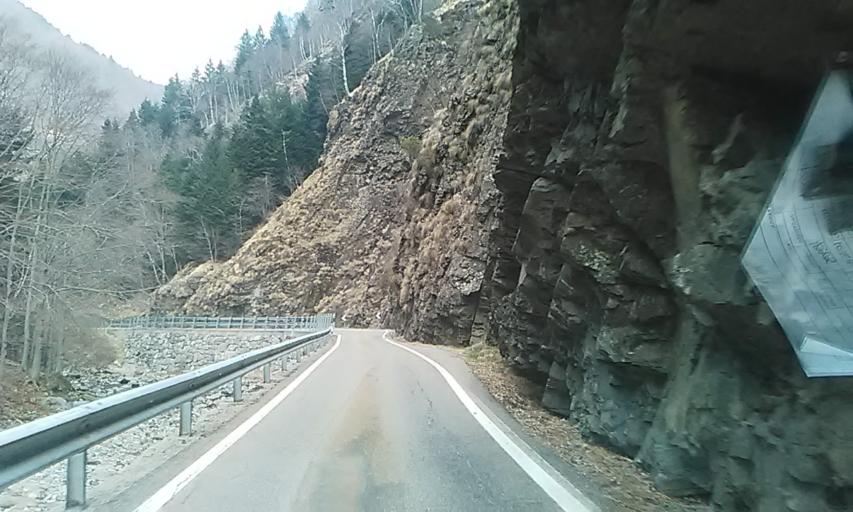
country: IT
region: Piedmont
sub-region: Provincia di Vercelli
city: Cervatto
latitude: 45.8899
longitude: 8.1787
